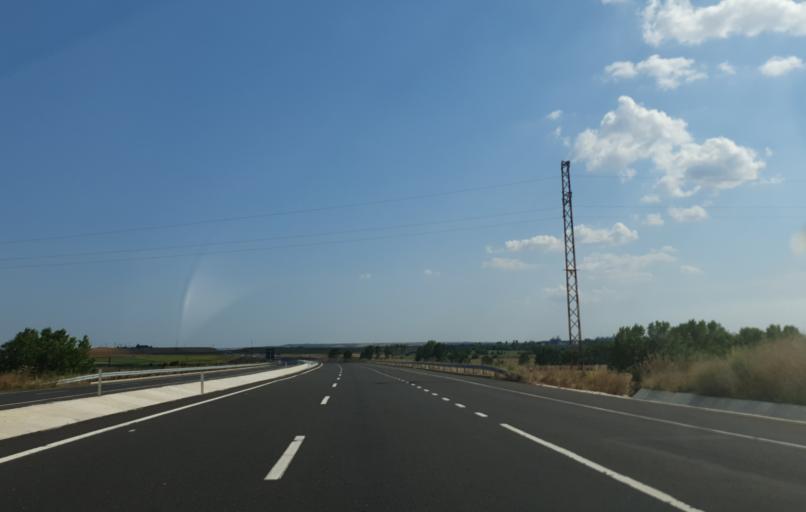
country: TR
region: Tekirdag
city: Muratli
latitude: 41.2236
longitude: 27.5319
